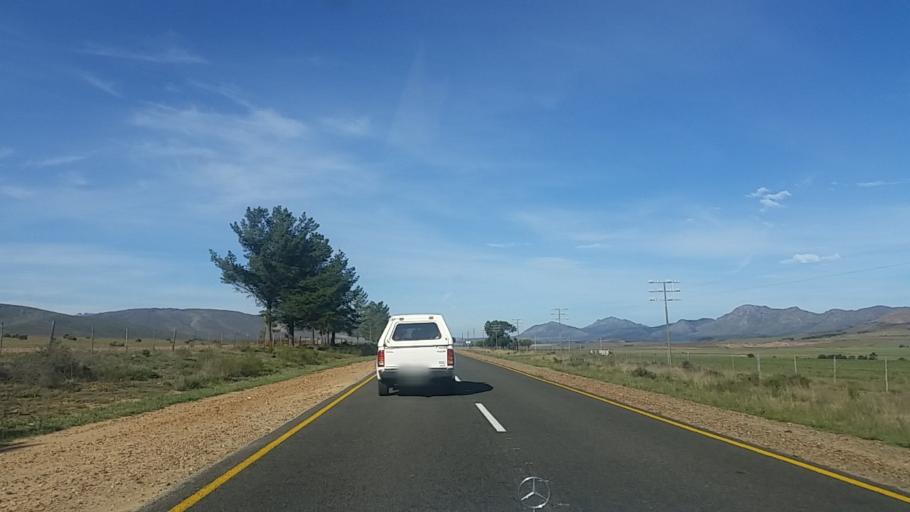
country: ZA
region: Western Cape
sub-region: Eden District Municipality
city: George
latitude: -33.8180
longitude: 22.5054
